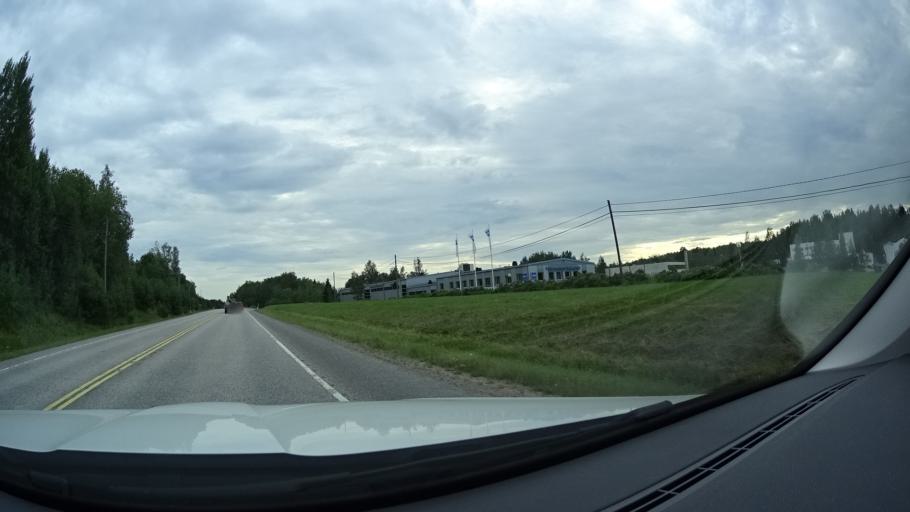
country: FI
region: Uusimaa
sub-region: Helsinki
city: Kirkkonummi
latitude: 60.1629
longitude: 24.5440
